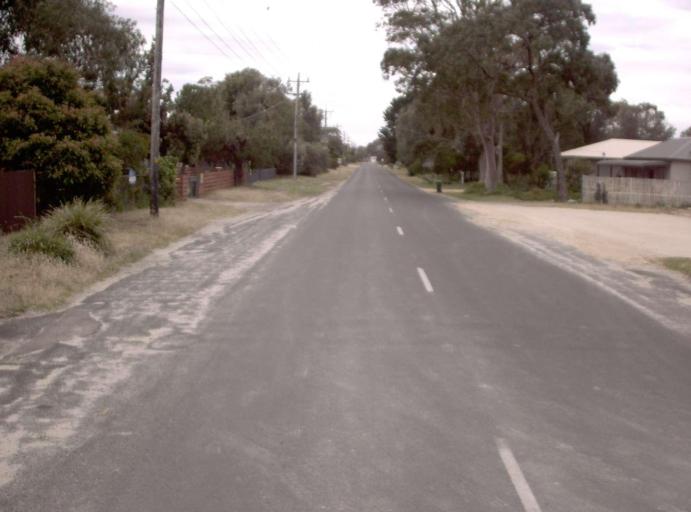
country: AU
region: Victoria
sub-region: East Gippsland
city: Bairnsdale
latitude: -38.0575
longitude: 147.5685
